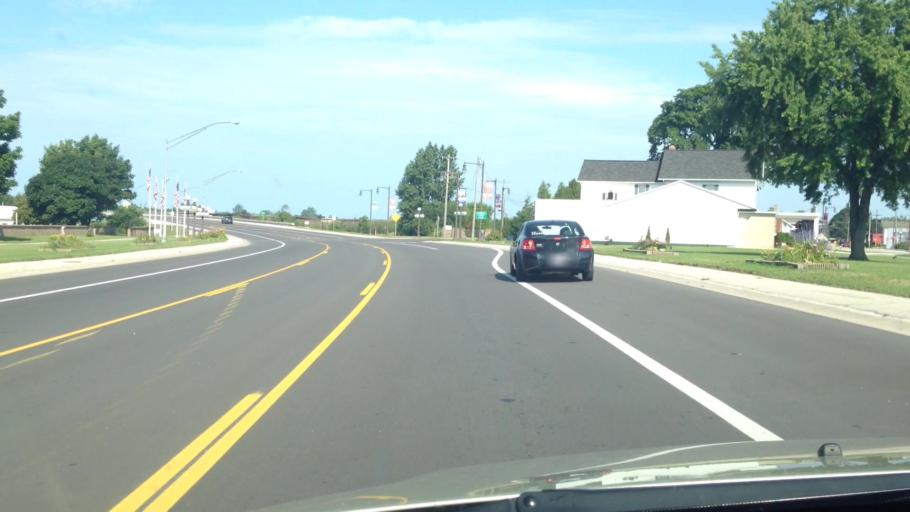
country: US
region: Michigan
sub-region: Schoolcraft County
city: Manistique
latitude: 45.9532
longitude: -86.2454
